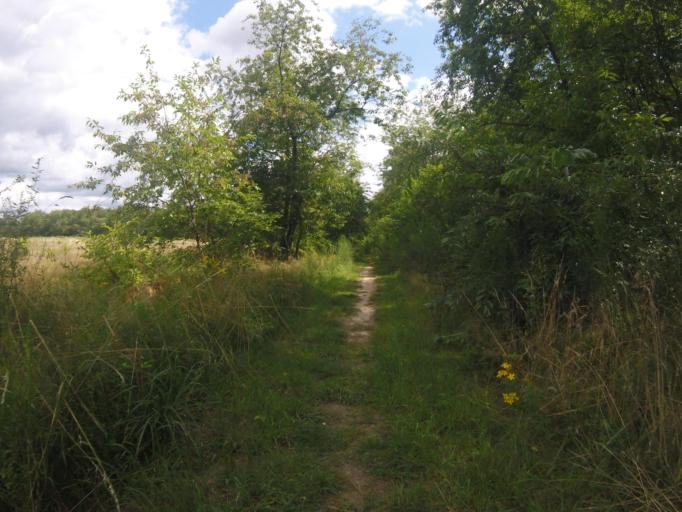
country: DE
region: Brandenburg
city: Konigs Wusterhausen
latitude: 52.3071
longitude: 13.6104
